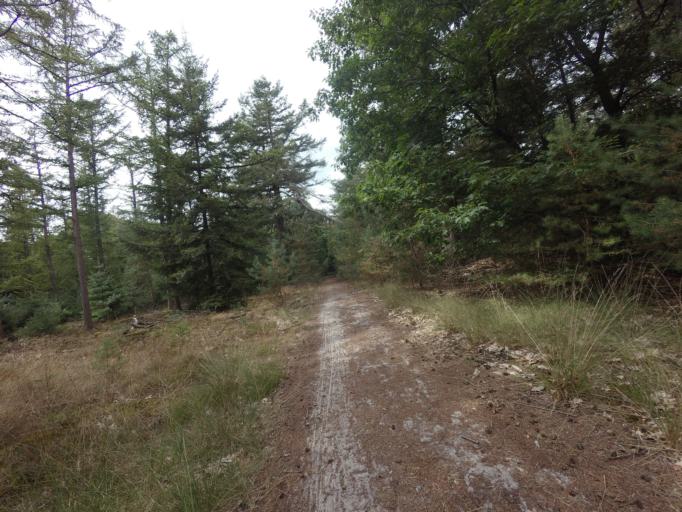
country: NL
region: North Brabant
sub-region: Gemeente Landerd
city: Schaijk
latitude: 51.7145
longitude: 5.6251
